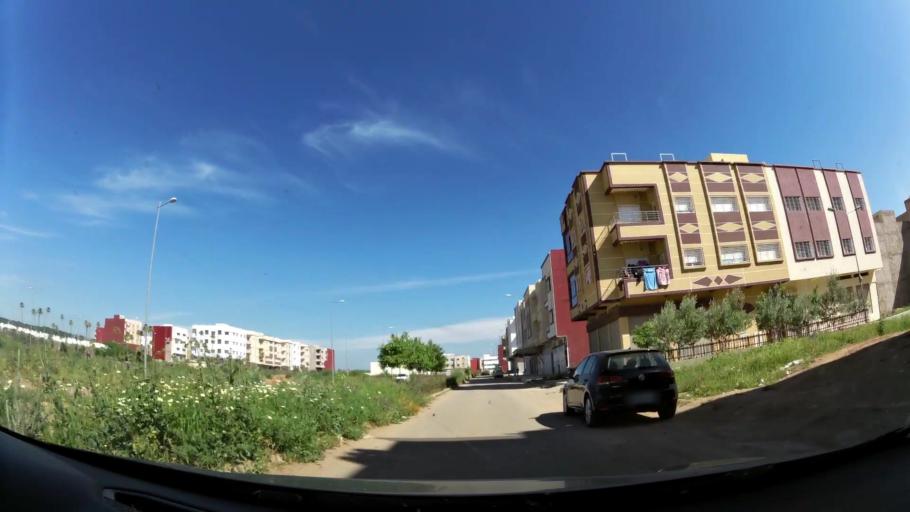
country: MA
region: Fes-Boulemane
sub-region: Fes
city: Fes
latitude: 33.9957
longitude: -5.0089
